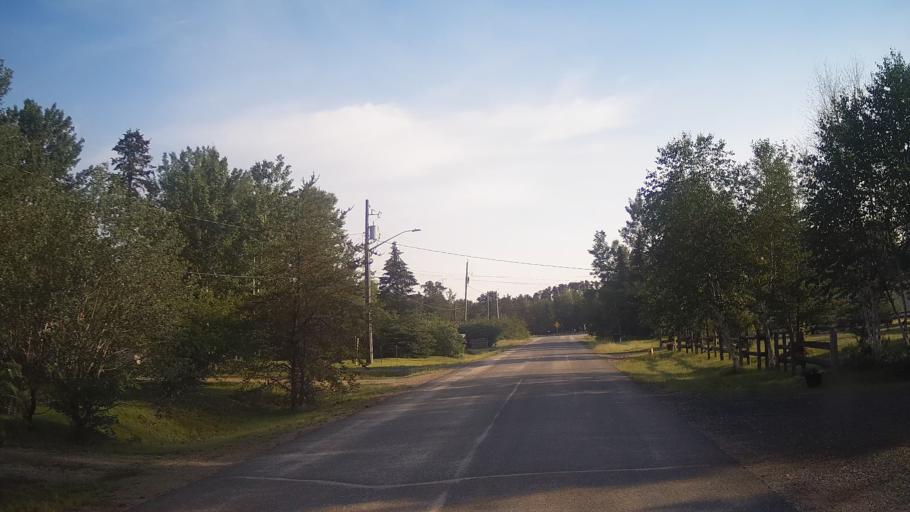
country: CA
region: Ontario
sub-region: Rainy River District
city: Atikokan
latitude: 49.4145
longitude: -91.6555
